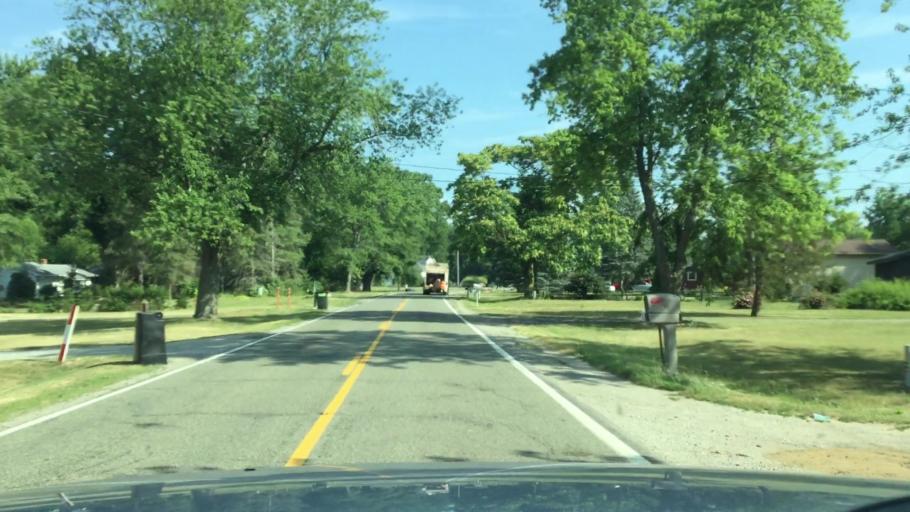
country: US
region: Michigan
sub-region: Genesee County
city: Montrose
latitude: 43.1309
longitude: -83.8588
